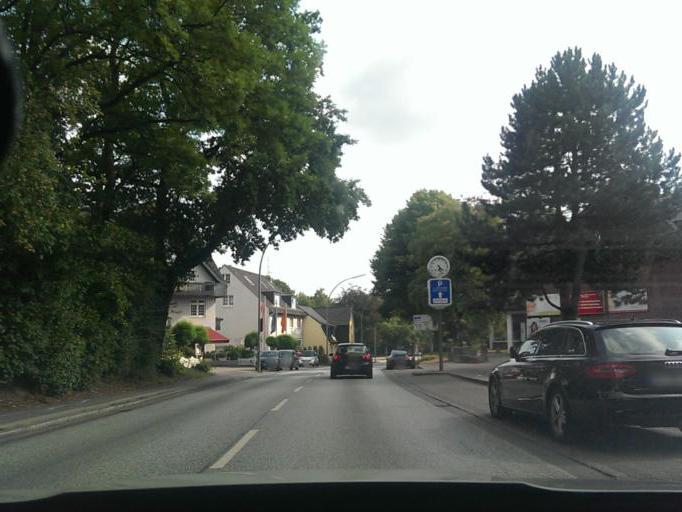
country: DE
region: Hamburg
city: Poppenbuettel
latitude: 53.6588
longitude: 10.0850
